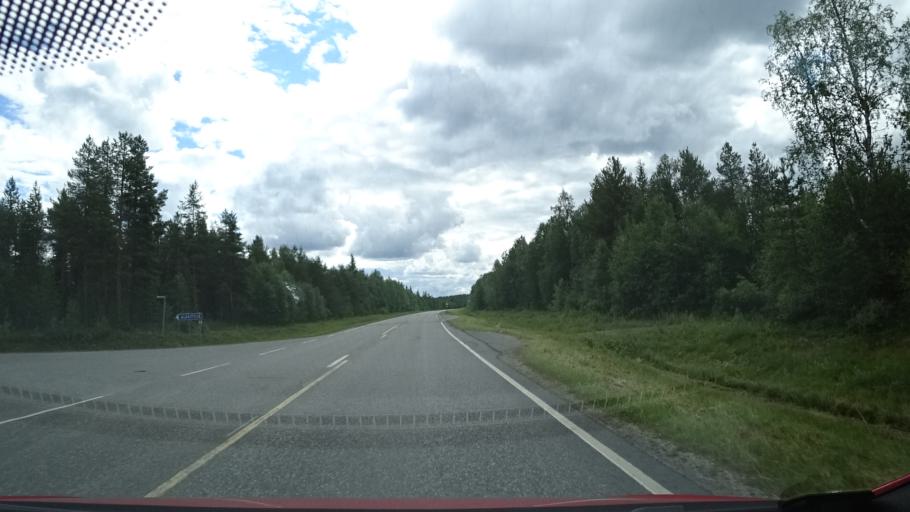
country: FI
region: Lapland
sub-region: Tunturi-Lappi
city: Kittilae
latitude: 67.6280
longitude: 24.9326
